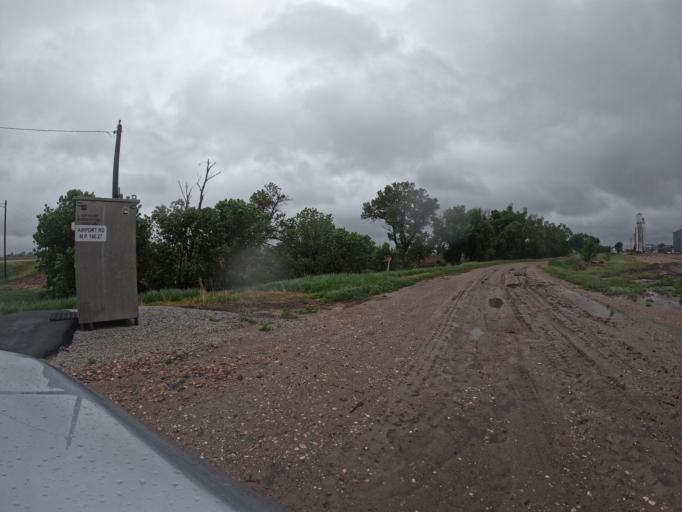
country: US
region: Nebraska
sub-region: Clay County
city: Harvard
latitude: 40.6162
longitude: -98.0901
